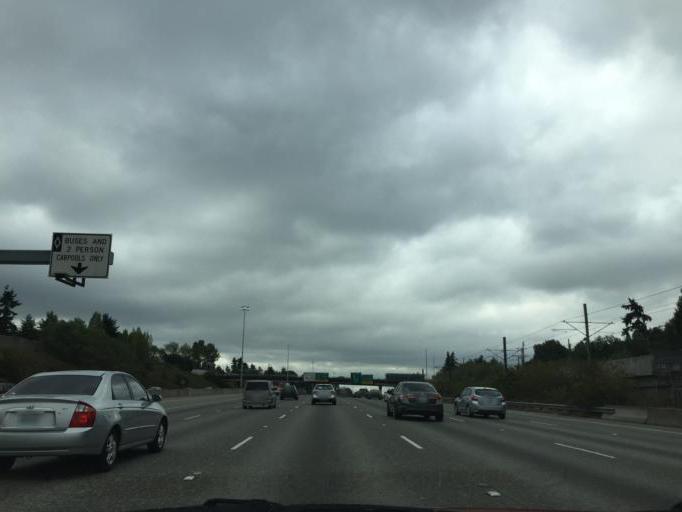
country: US
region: Washington
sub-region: King County
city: Tukwila
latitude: 47.4761
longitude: -122.2709
